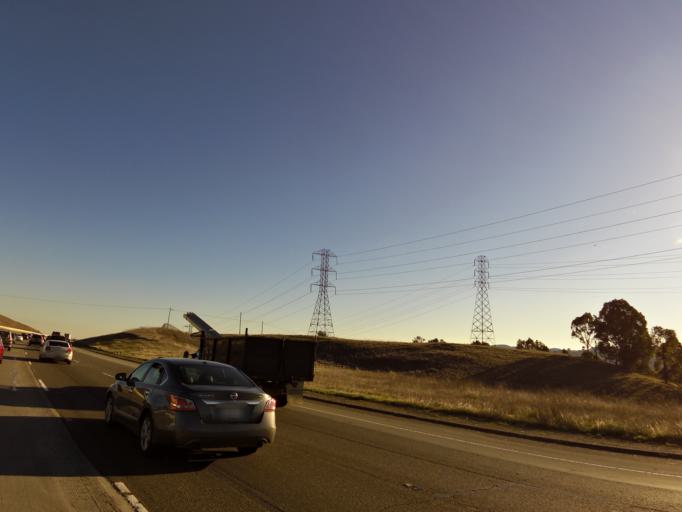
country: US
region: California
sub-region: Santa Clara County
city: Morgan Hill
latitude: 37.1863
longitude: -121.6873
